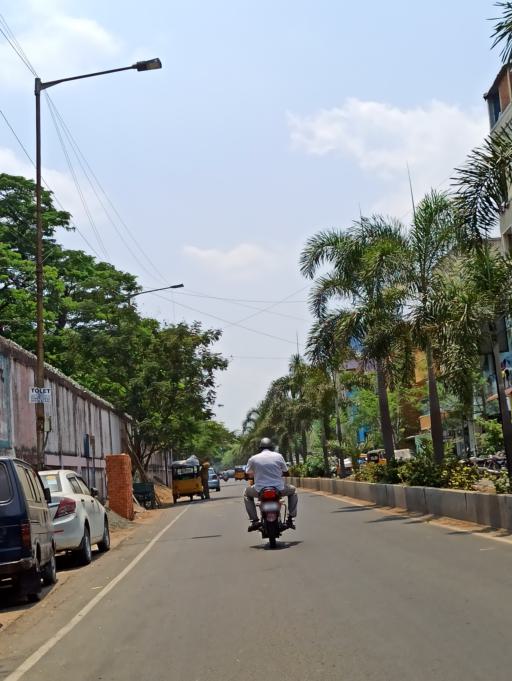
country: IN
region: Tamil Nadu
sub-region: Chennai
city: Chetput
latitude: 13.0927
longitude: 80.2384
